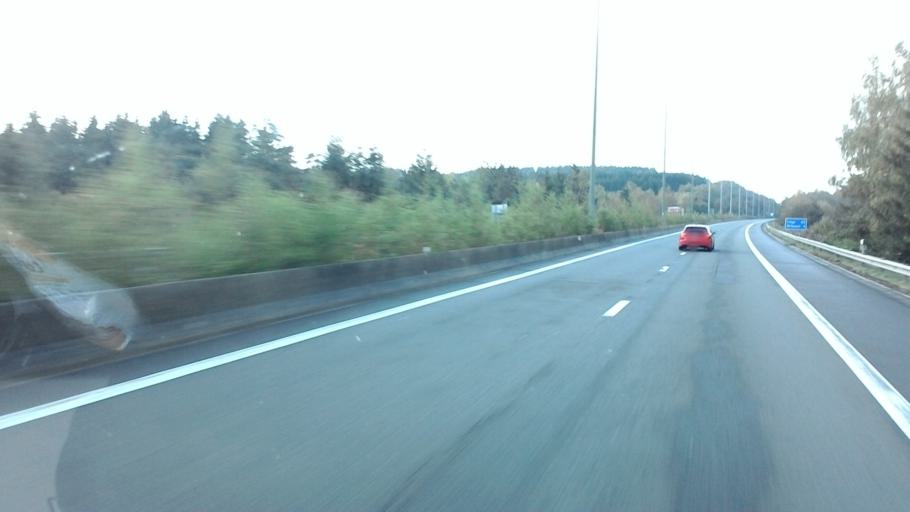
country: BE
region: Wallonia
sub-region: Province du Luxembourg
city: Manhay
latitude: 50.3156
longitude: 5.7077
